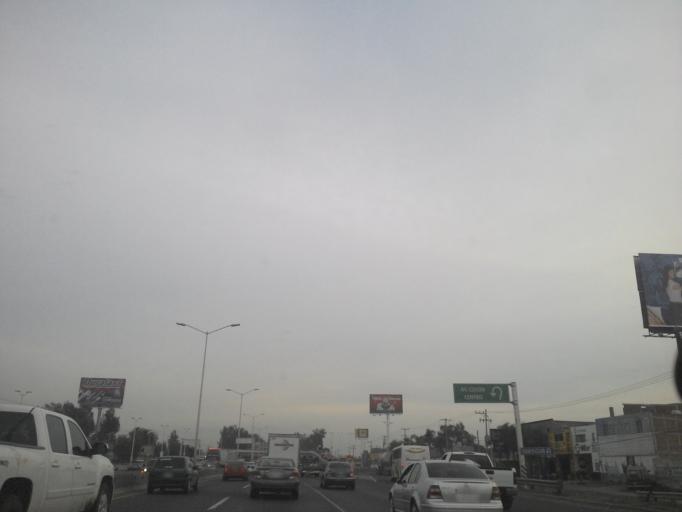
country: MX
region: Jalisco
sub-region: San Pedro Tlaquepaque
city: Paseo del Prado
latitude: 20.6031
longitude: -103.3976
